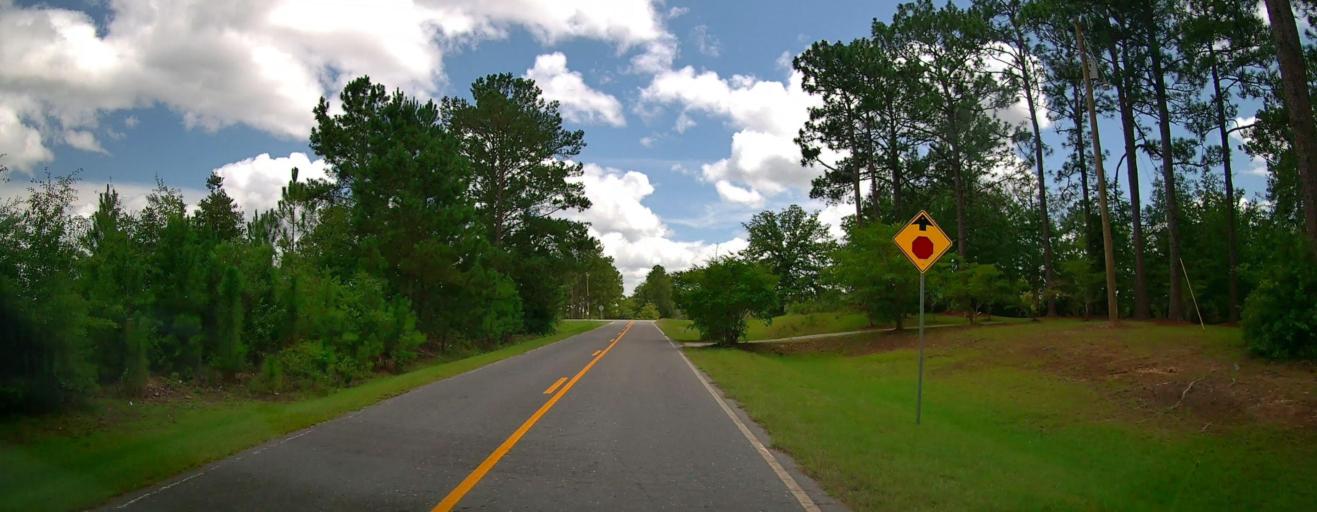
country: US
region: Georgia
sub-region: Irwin County
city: Ocilla
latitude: 31.6452
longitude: -83.3959
